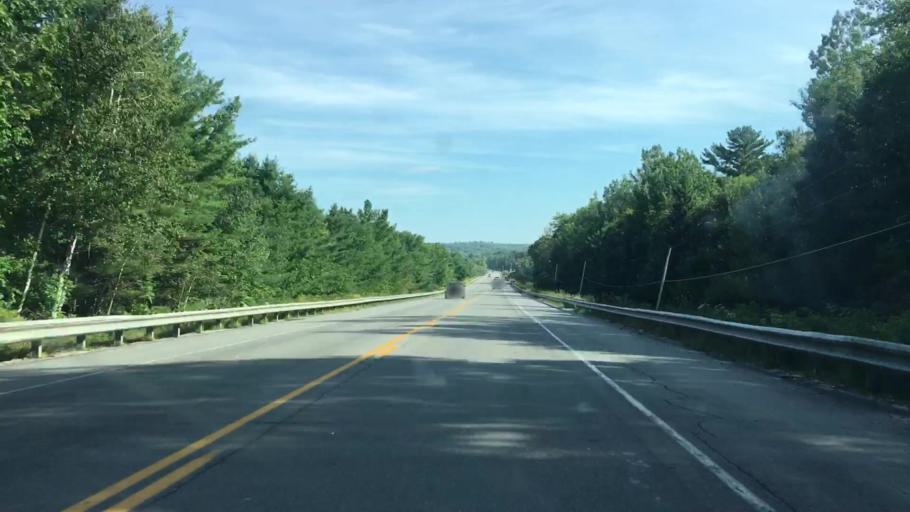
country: US
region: Maine
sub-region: Penobscot County
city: Lincoln
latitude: 45.3672
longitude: -68.5529
